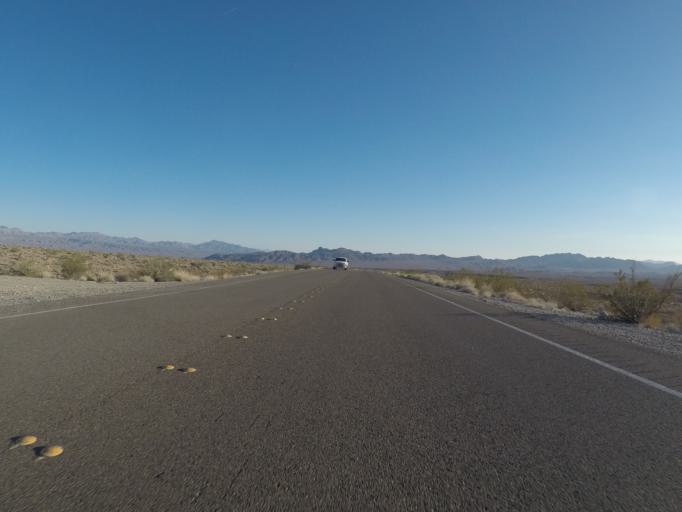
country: US
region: Nevada
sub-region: Clark County
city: Moapa Valley
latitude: 36.3575
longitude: -114.4834
